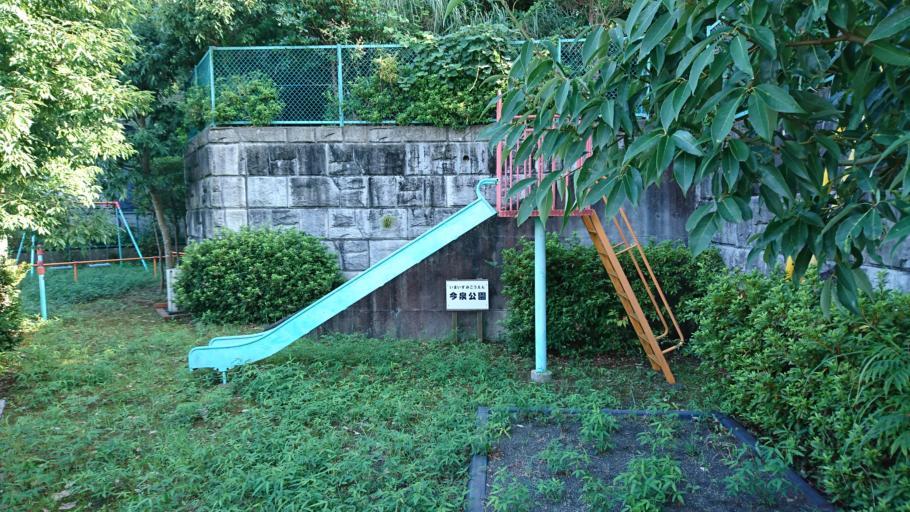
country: JP
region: Shizuoka
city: Shizuoka-shi
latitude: 35.0040
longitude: 138.4623
